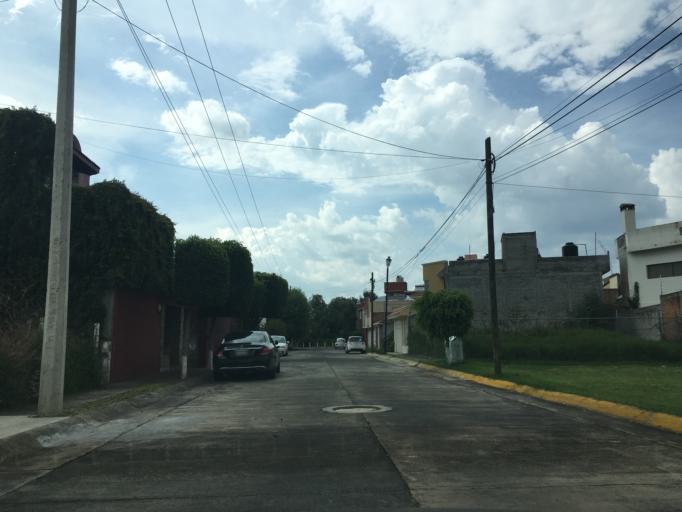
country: MX
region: Michoacan
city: Morelia
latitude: 19.6821
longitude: -101.2108
